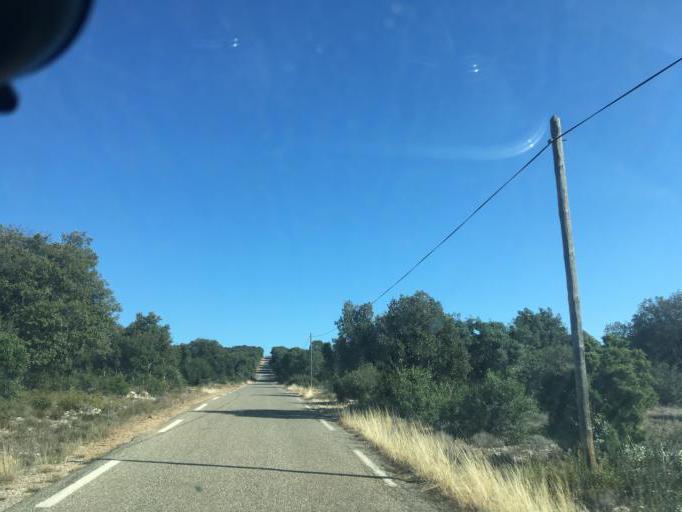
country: FR
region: Provence-Alpes-Cote d'Azur
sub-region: Departement du Var
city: Regusse
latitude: 43.7287
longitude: 6.1165
